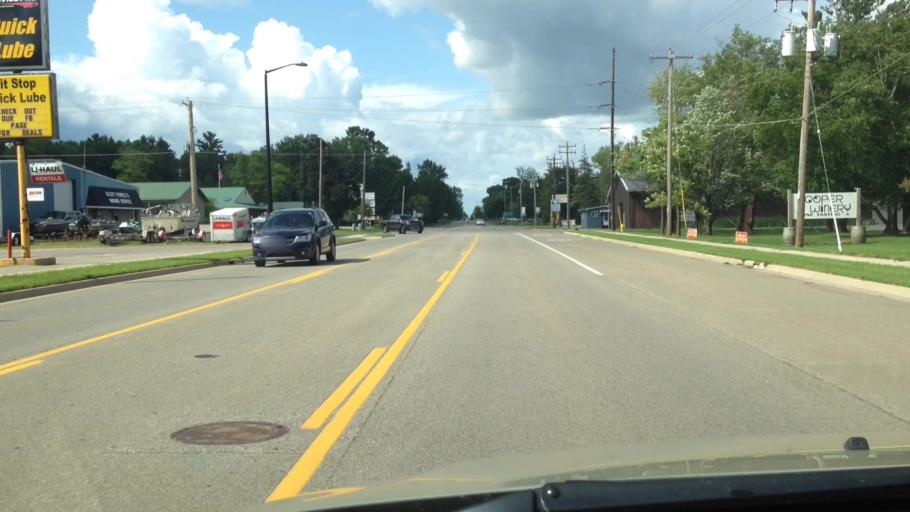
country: US
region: Michigan
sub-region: Menominee County
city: Menominee
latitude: 45.1432
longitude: -87.6120
